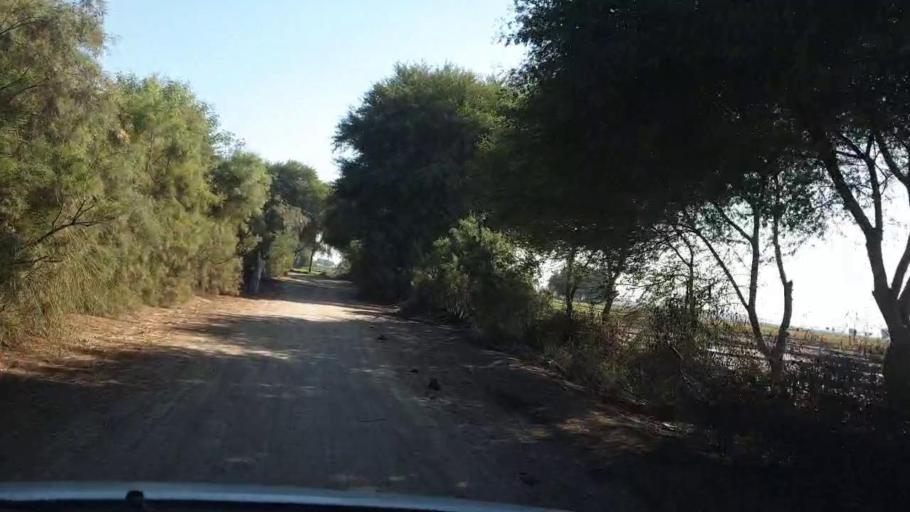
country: PK
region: Sindh
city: Dadu
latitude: 26.7959
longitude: 67.8322
